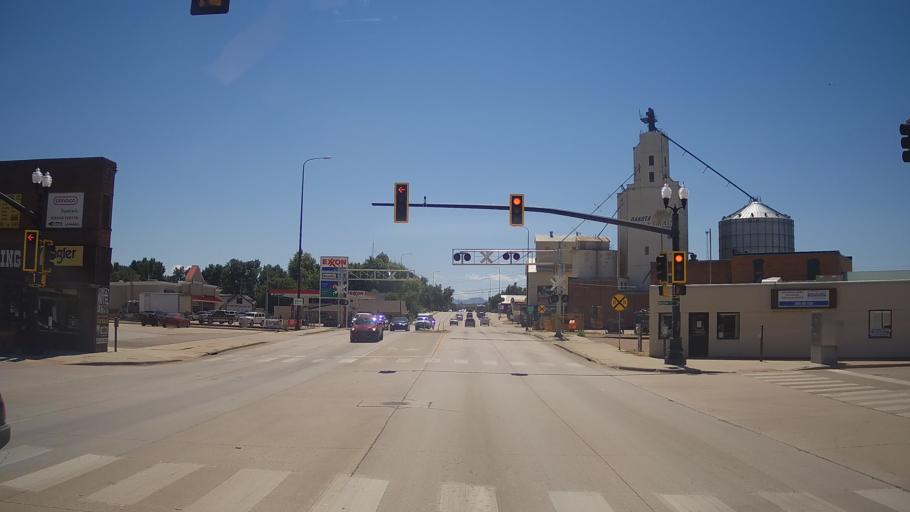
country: US
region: South Dakota
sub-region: Butte County
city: Belle Fourche
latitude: 44.6716
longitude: -103.8536
